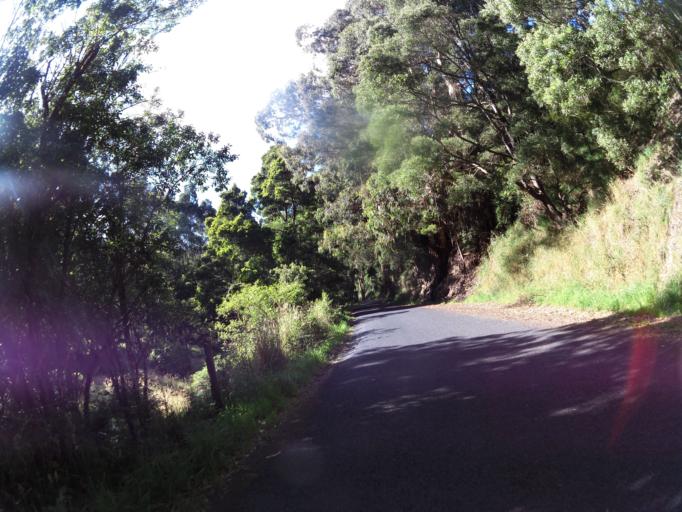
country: AU
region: Victoria
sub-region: Colac-Otway
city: Apollo Bay
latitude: -38.7583
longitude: 143.6263
